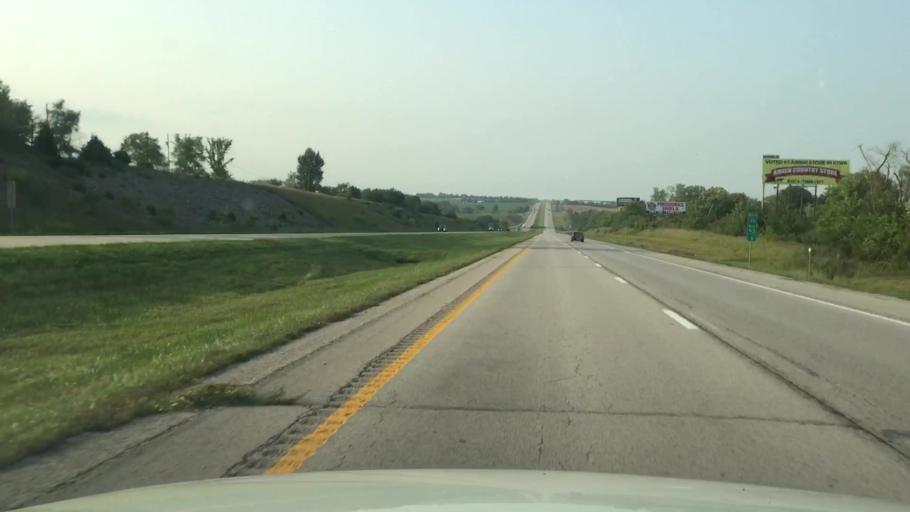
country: US
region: Missouri
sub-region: Harrison County
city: Bethany
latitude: 40.2850
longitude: -94.0122
